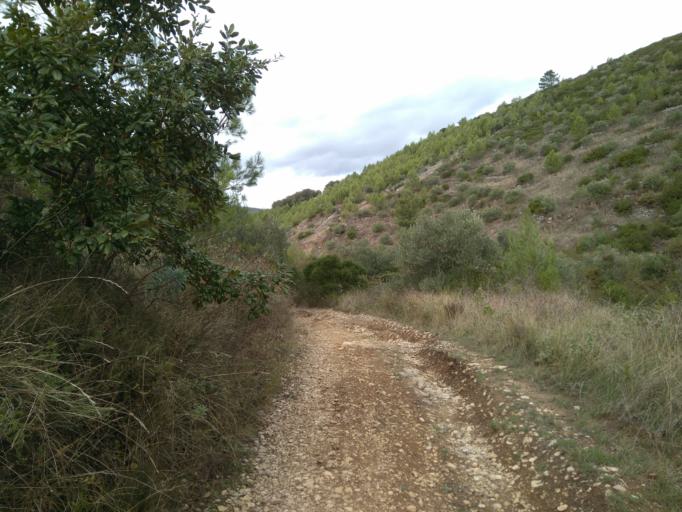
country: PT
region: Leiria
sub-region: Porto de Mos
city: Porto de Mos
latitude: 39.5783
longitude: -8.8132
